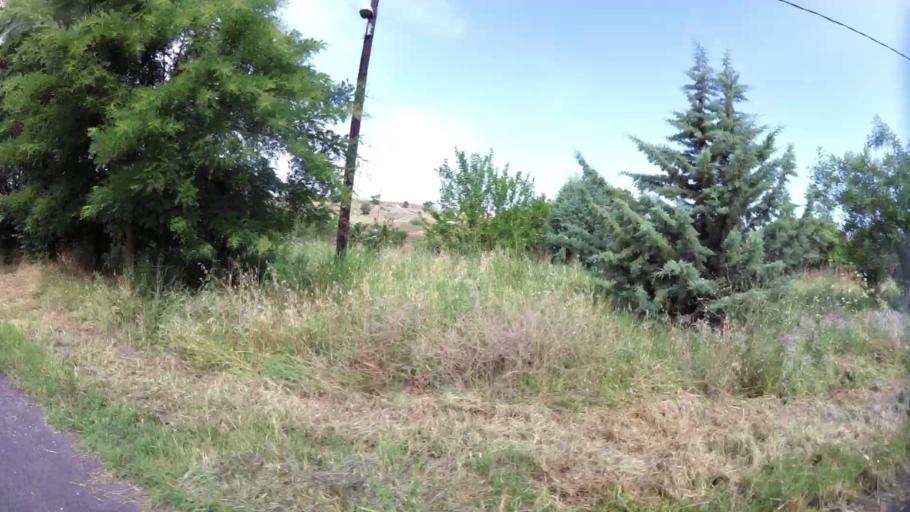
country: GR
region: Central Macedonia
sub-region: Nomos Thessalonikis
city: Panorama
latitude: 40.5748
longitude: 23.0057
